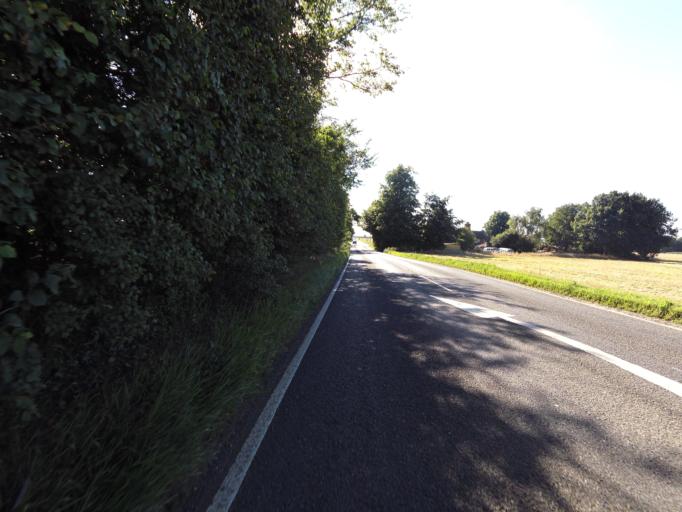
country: GB
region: England
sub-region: Suffolk
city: Kesgrave
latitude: 52.0507
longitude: 1.2560
